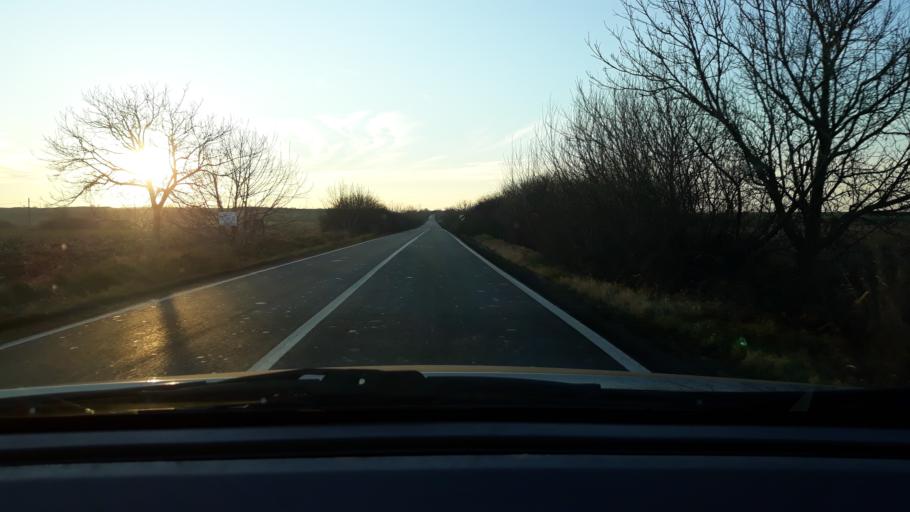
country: RO
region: Bihor
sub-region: Comuna Spinus
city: Spinus
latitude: 47.2300
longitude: 22.1820
